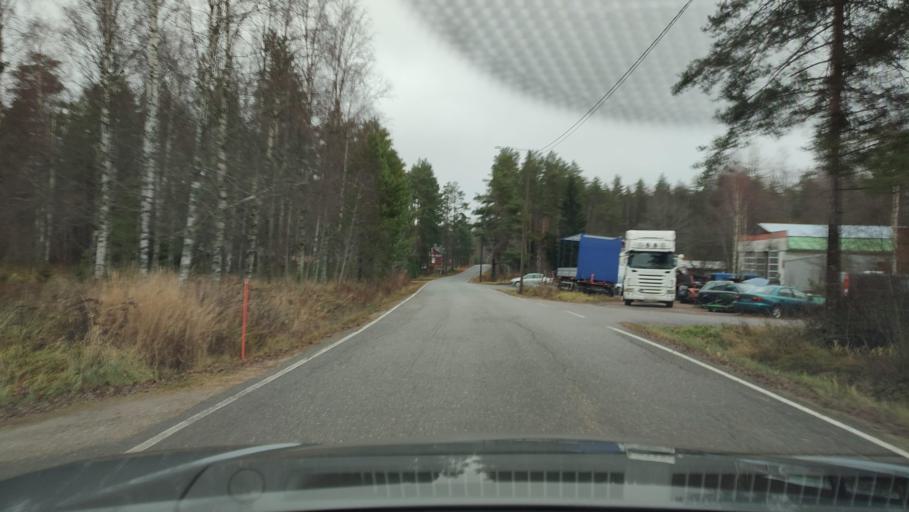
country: FI
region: Southern Ostrobothnia
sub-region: Suupohja
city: Isojoki
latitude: 62.1580
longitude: 21.8809
